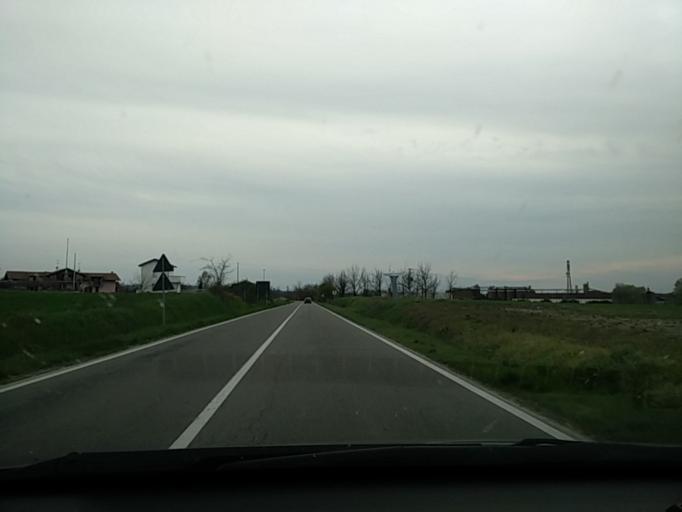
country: IT
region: Lombardy
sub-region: Provincia di Pavia
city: Retorbido
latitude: 44.9520
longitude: 9.0319
